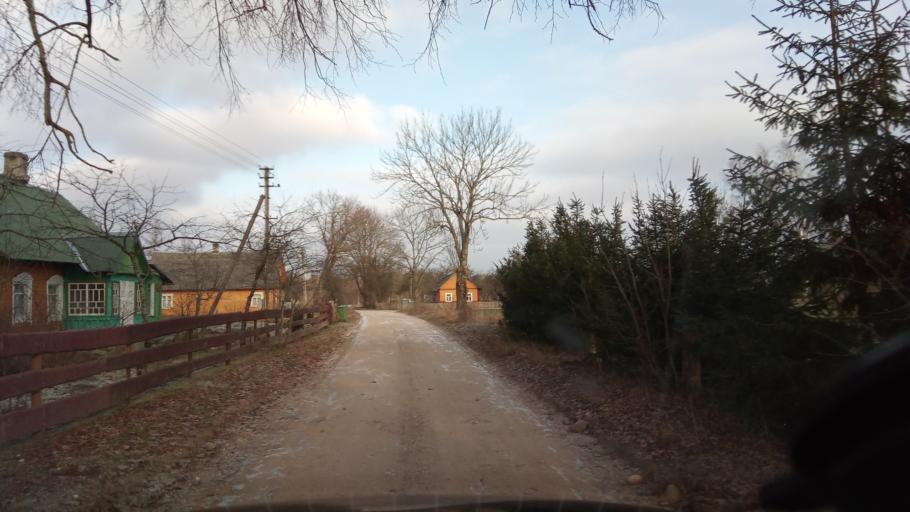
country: LT
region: Alytaus apskritis
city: Varena
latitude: 54.1278
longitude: 24.6465
